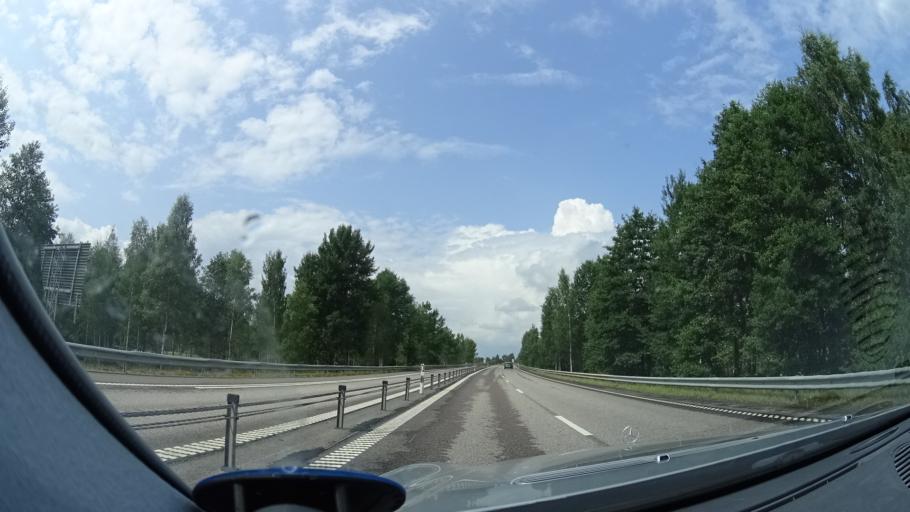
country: SE
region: Kalmar
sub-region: Nybro Kommun
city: Nybro
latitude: 56.7303
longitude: 15.8805
